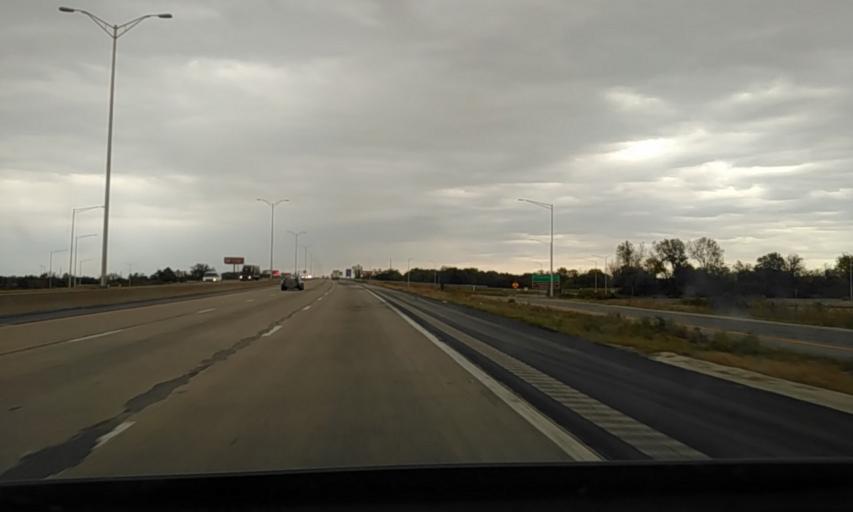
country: US
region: Illinois
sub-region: Saint Clair County
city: Centreville
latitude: 38.5635
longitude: -90.1330
